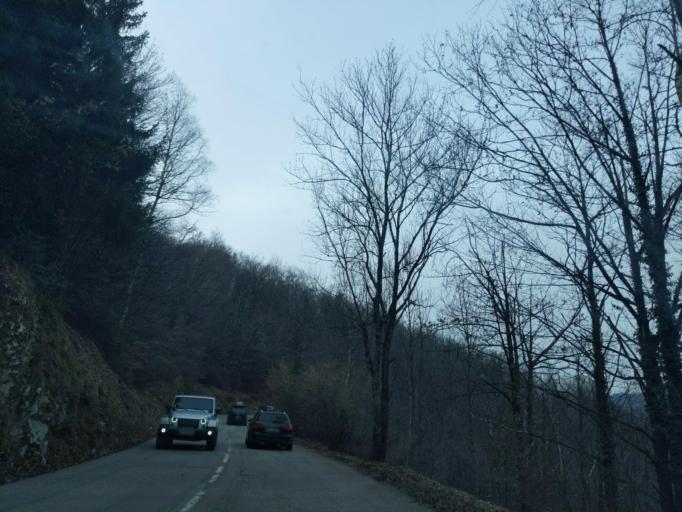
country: FR
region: Rhone-Alpes
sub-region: Departement de la Savoie
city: La Bathie
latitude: 45.6064
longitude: 6.4399
